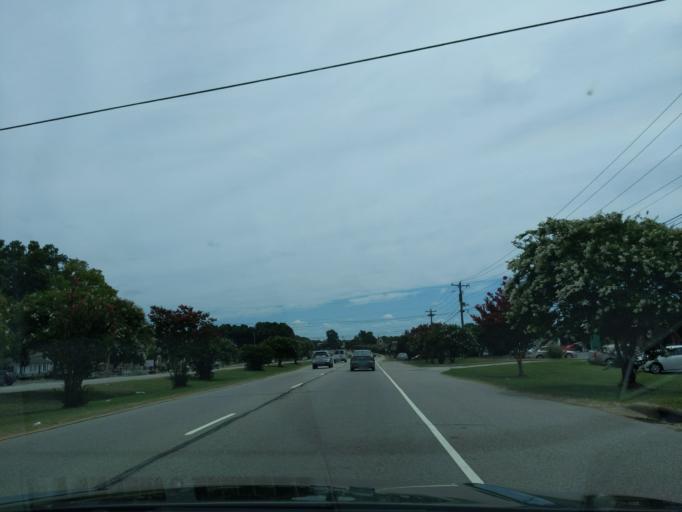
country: US
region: North Carolina
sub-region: Cabarrus County
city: Harrisburg
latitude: 35.3154
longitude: -80.6824
